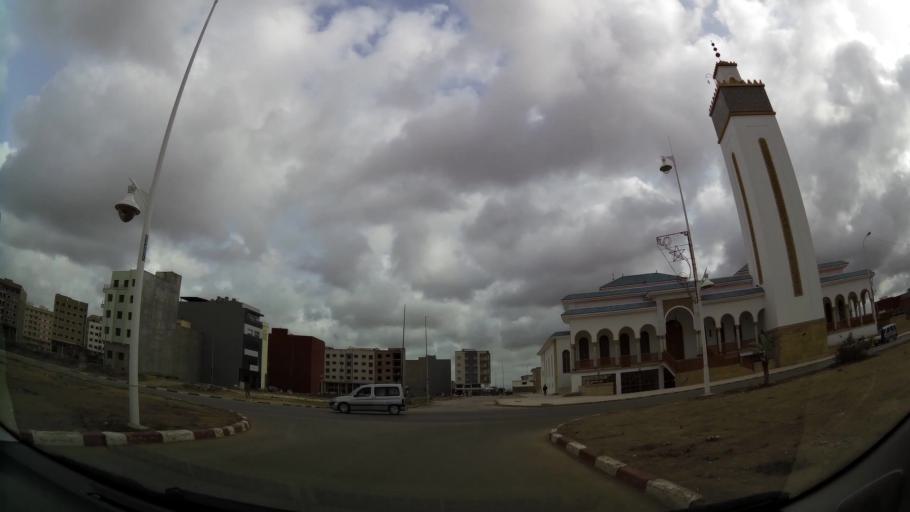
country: MA
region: Oriental
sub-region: Nador
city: Nador
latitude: 35.1529
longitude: -2.9184
